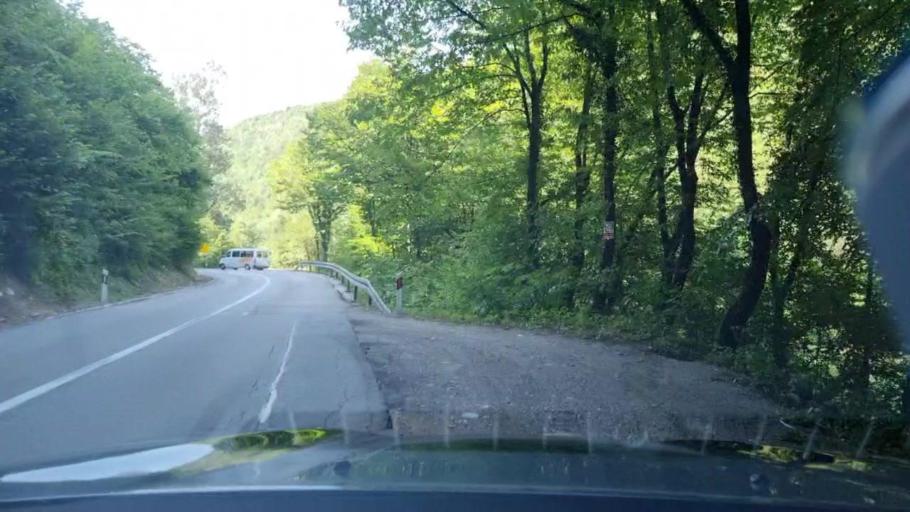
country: BA
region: Federation of Bosnia and Herzegovina
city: Stijena
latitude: 44.8939
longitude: 16.0475
